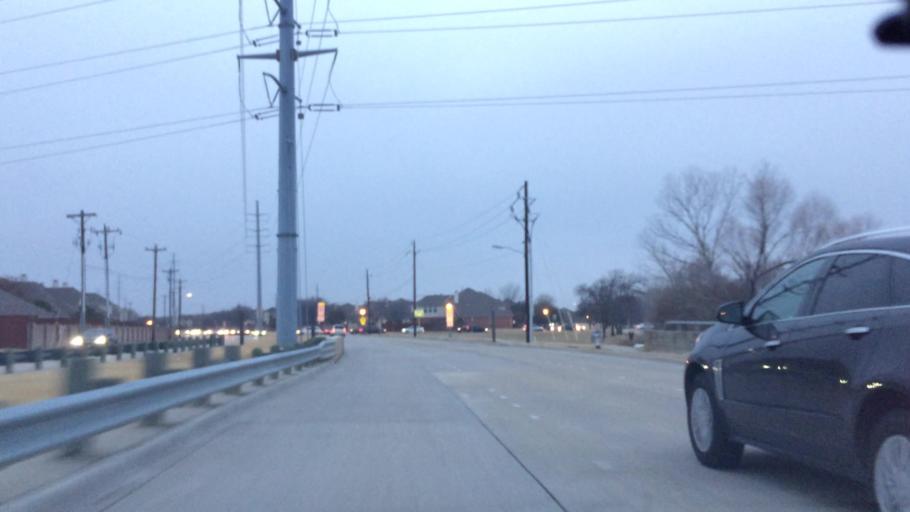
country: US
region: Texas
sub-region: Collin County
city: Frisco
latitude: 33.1008
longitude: -96.7750
